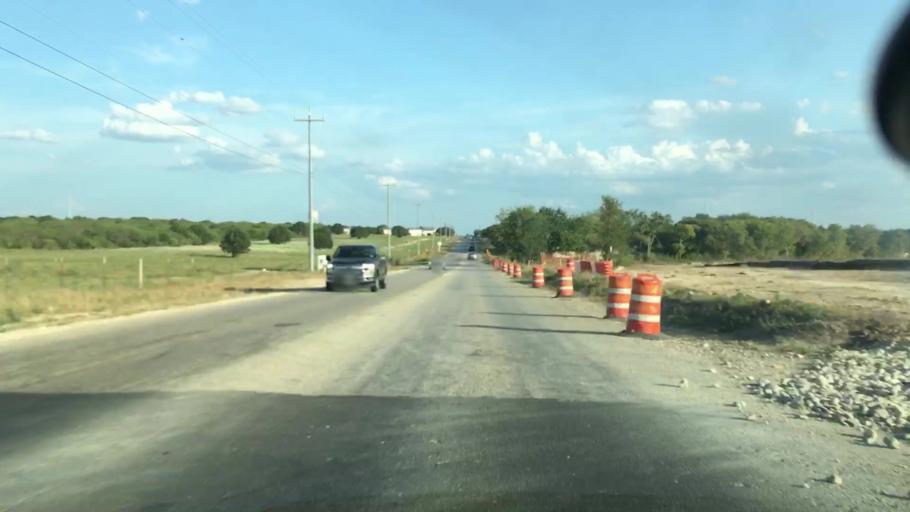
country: US
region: Texas
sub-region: Guadalupe County
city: Northcliff
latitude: 29.6073
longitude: -98.2652
